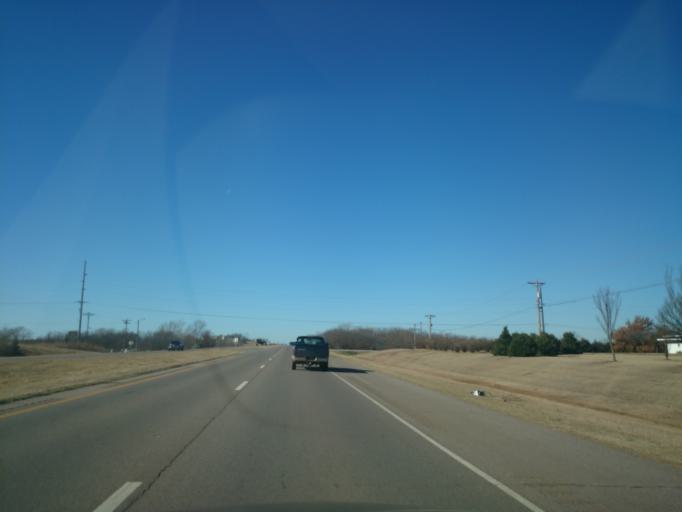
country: US
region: Oklahoma
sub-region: Payne County
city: Stillwater
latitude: 36.1161
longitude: -97.1387
